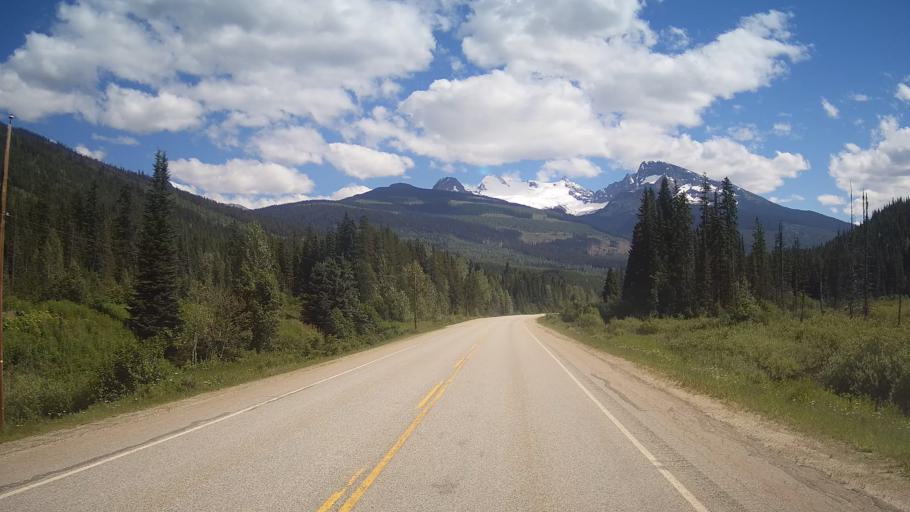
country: CA
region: Alberta
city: Jasper Park Lodge
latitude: 52.5965
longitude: -119.1035
